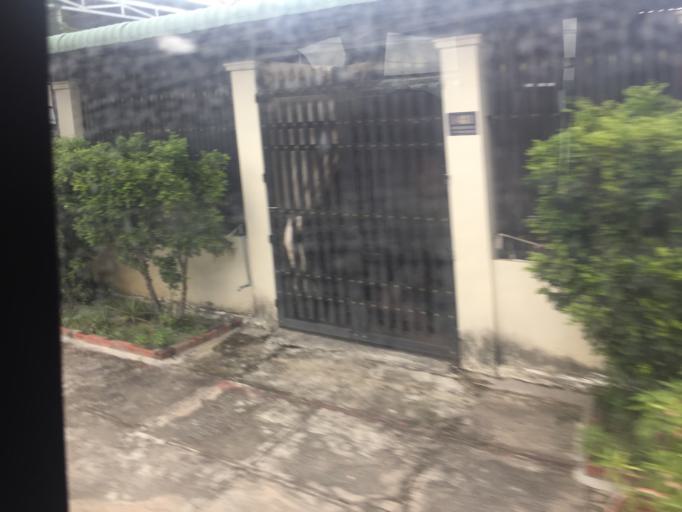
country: VN
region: Ho Chi Minh City
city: Cu Chi
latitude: 11.1266
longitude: 106.4823
